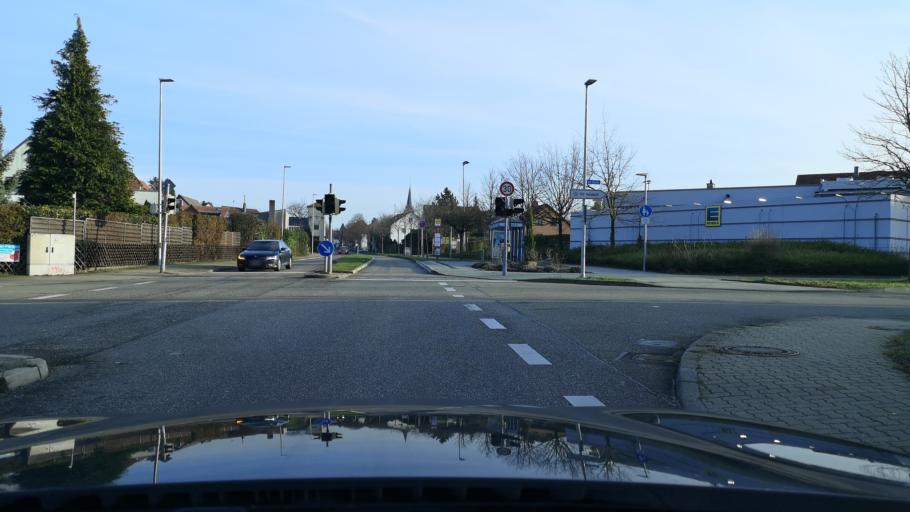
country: DE
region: Baden-Wuerttemberg
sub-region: Karlsruhe Region
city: Ettlingen
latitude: 48.9475
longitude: 8.4776
